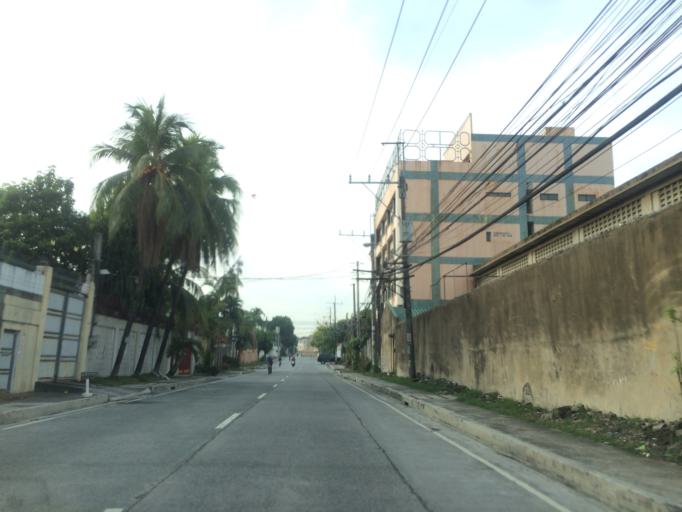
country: PH
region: Calabarzon
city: Del Monte
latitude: 14.6314
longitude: 121.0052
